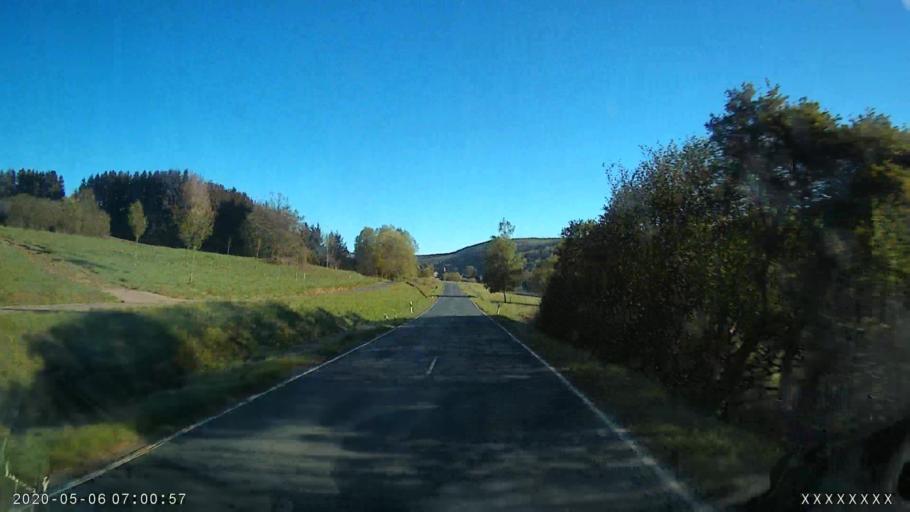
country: DE
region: Hesse
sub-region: Regierungsbezirk Giessen
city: Haiger
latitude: 50.7840
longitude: 8.2052
